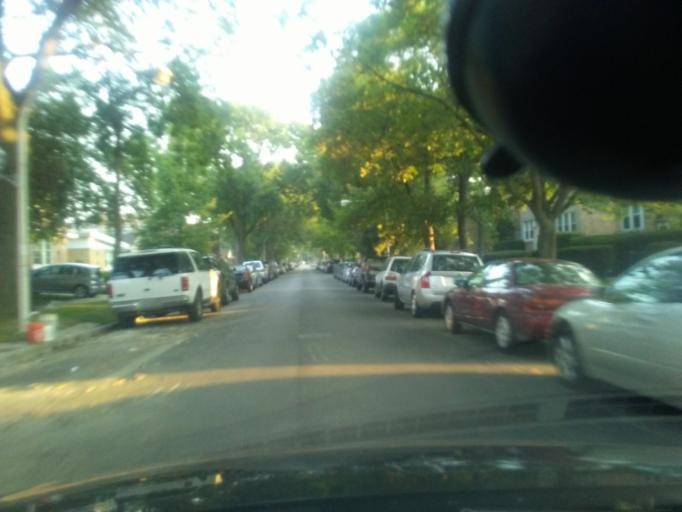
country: US
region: Illinois
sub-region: Cook County
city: Lincolnwood
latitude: 41.9780
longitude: -87.7035
